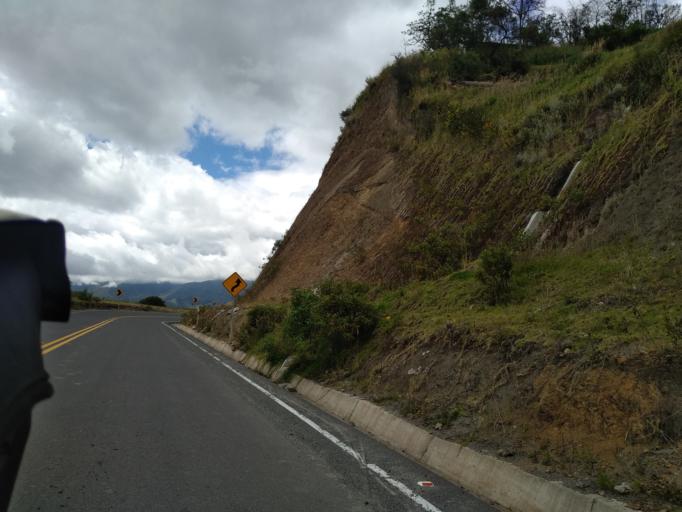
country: EC
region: Cotopaxi
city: Saquisili
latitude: -0.7605
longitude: -78.9110
